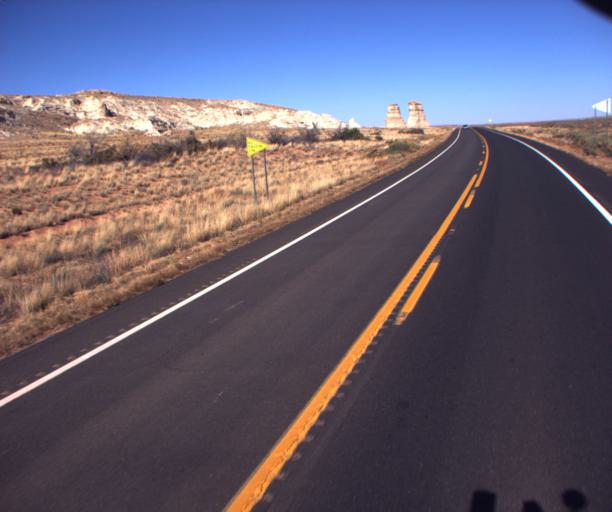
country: US
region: Arizona
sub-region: Coconino County
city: Kaibito
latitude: 36.3279
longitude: -110.9268
